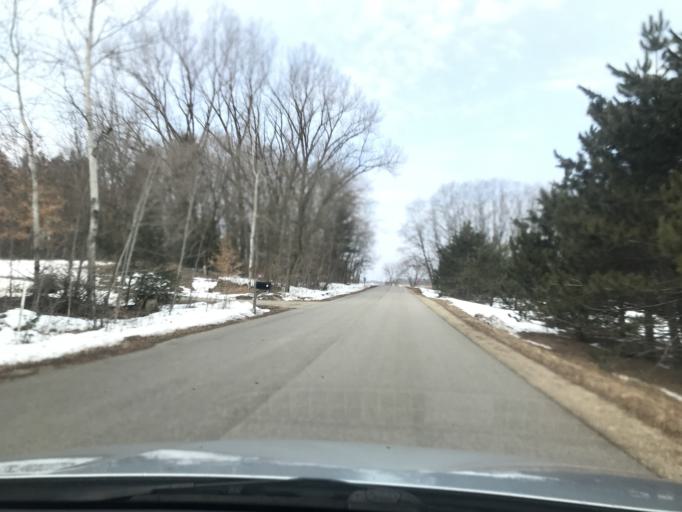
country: US
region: Wisconsin
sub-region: Oconto County
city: Oconto Falls
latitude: 44.8298
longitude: -88.1860
